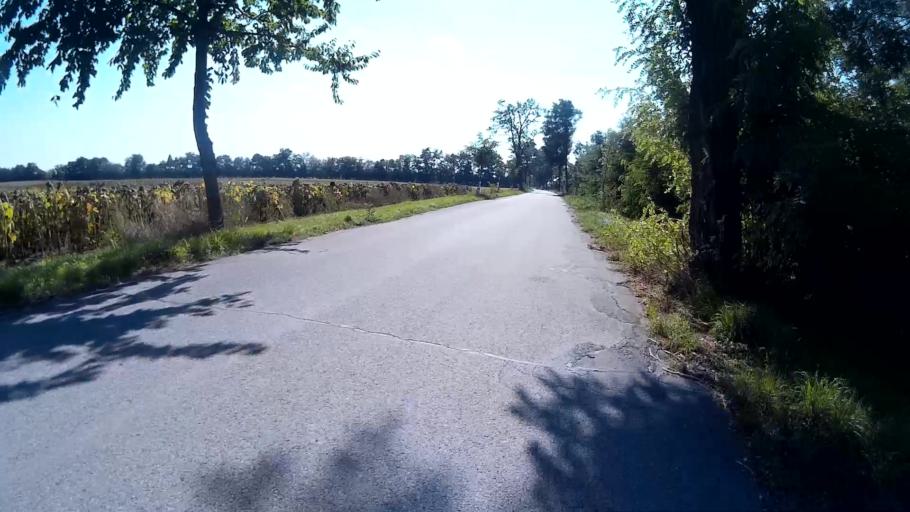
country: CZ
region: South Moravian
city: Novosedly
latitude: 48.7901
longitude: 16.4898
